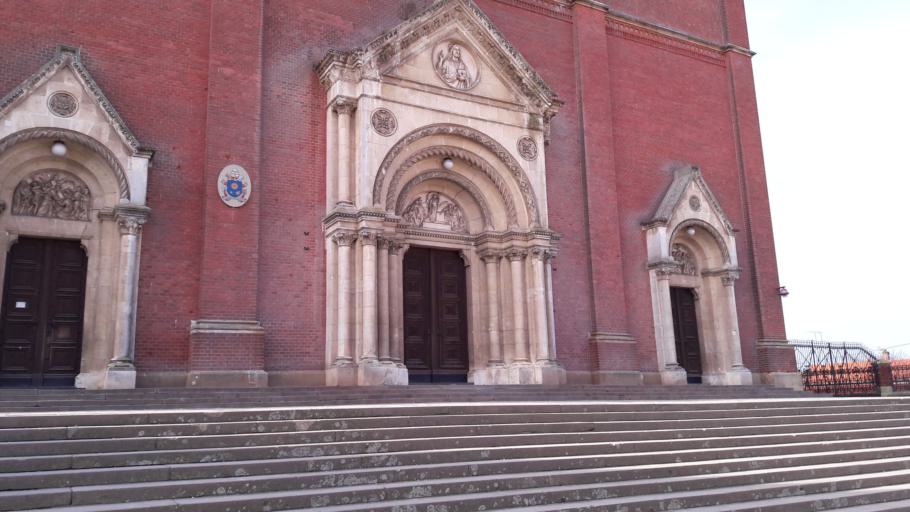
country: HR
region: Osjecko-Baranjska
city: Piskorevci
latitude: 45.3077
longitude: 18.4116
